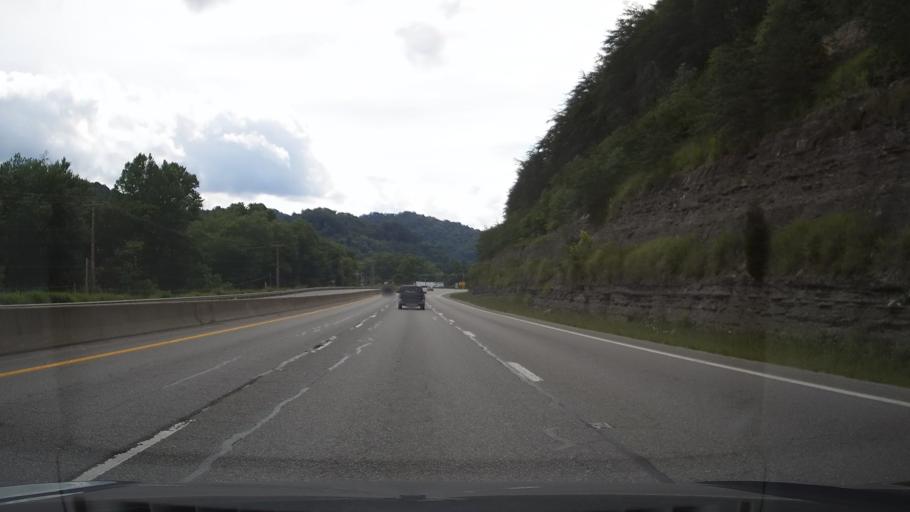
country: US
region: Kentucky
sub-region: Pike County
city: Coal Run Village
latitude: 37.5105
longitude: -82.5434
